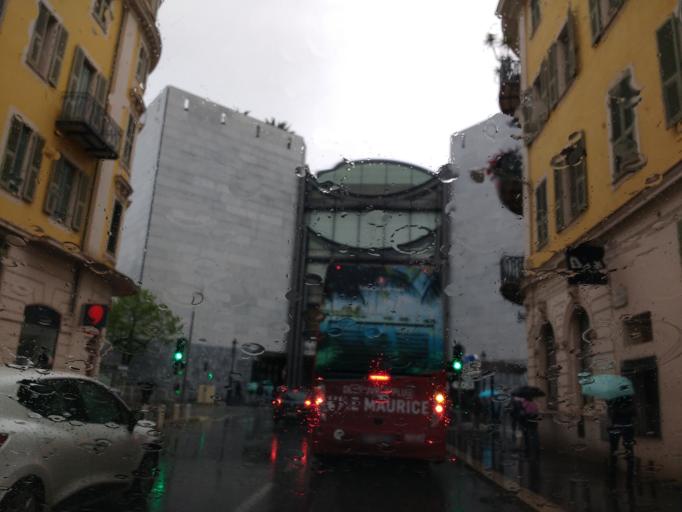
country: FR
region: Provence-Alpes-Cote d'Azur
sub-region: Departement des Alpes-Maritimes
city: Nice
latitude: 43.7012
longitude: 7.2794
